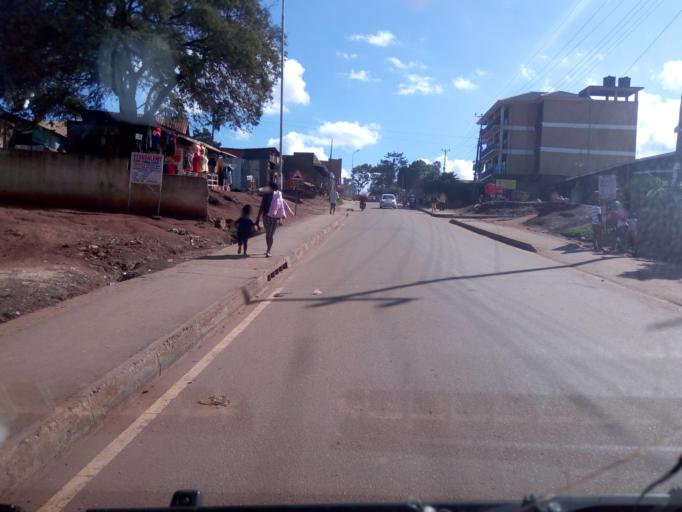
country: UG
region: Central Region
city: Kampala Central Division
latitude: 0.3330
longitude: 32.5574
